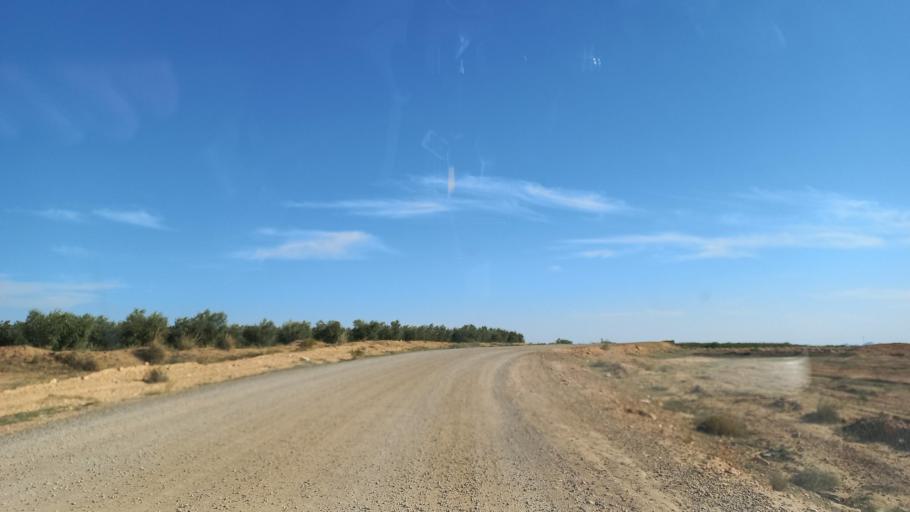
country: TN
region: Al Qasrayn
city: Sbiba
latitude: 35.2995
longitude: 9.0967
